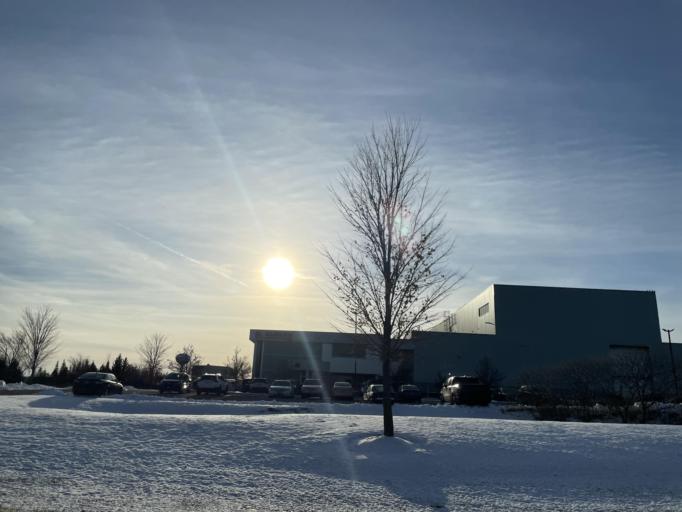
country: CA
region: Ontario
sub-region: Wellington County
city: Guelph
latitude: 43.5447
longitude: -80.2925
